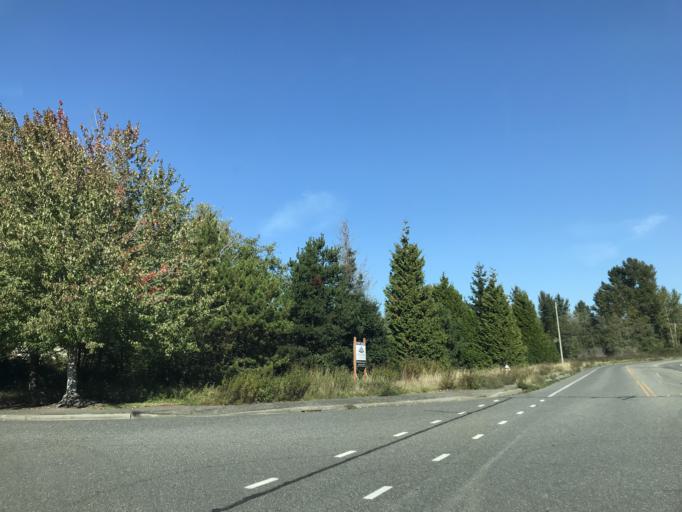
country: US
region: Washington
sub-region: Whatcom County
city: Bellingham
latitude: 48.8071
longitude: -122.4940
